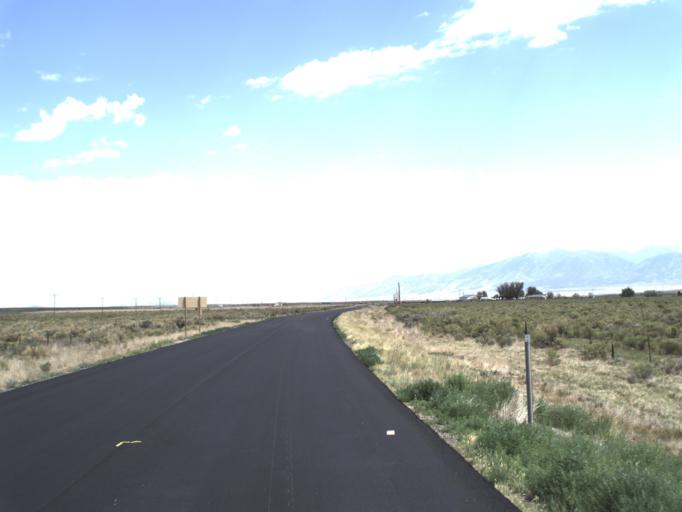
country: US
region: Utah
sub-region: Tooele County
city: Tooele
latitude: 40.1643
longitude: -112.4307
